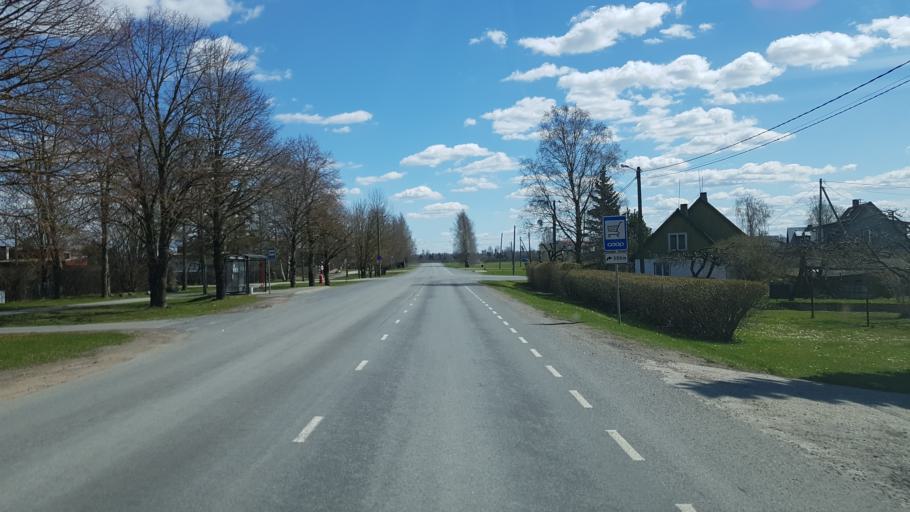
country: EE
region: Viljandimaa
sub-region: Viiratsi vald
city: Viiratsi
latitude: 58.3611
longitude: 25.6433
